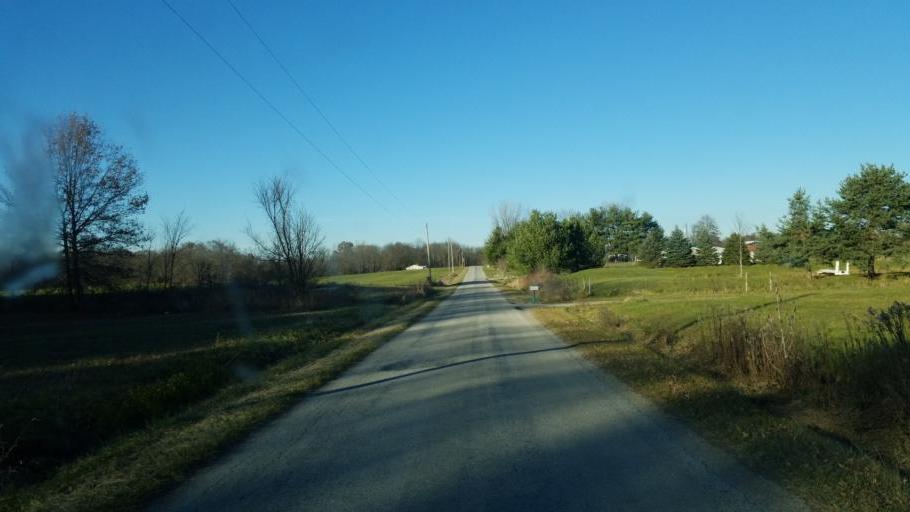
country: US
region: Ohio
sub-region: Morrow County
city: Cardington
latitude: 40.4542
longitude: -82.8862
